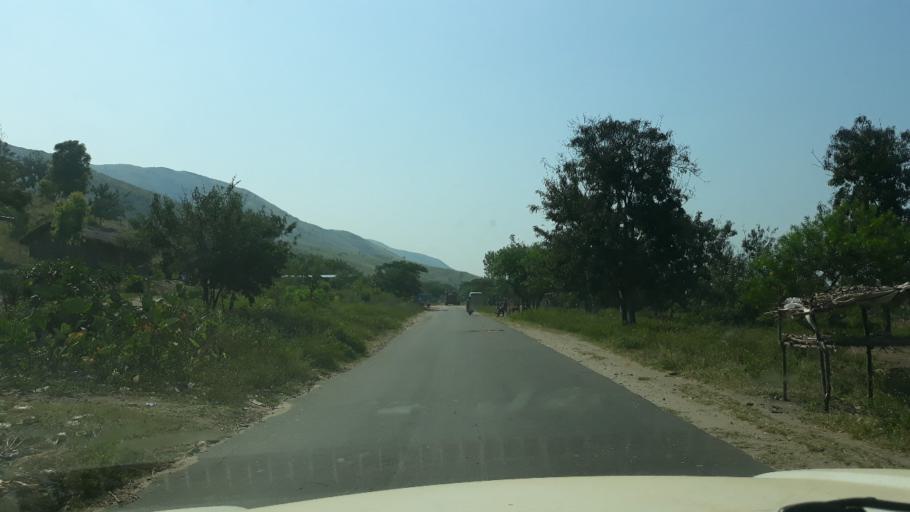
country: CD
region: South Kivu
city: Uvira
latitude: -3.2860
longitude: 29.1608
